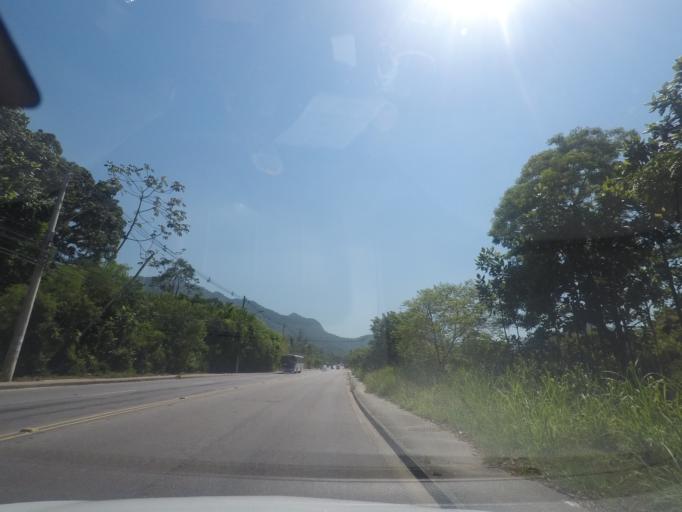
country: BR
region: Rio de Janeiro
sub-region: Nilopolis
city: Nilopolis
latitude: -22.9852
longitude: -43.4740
